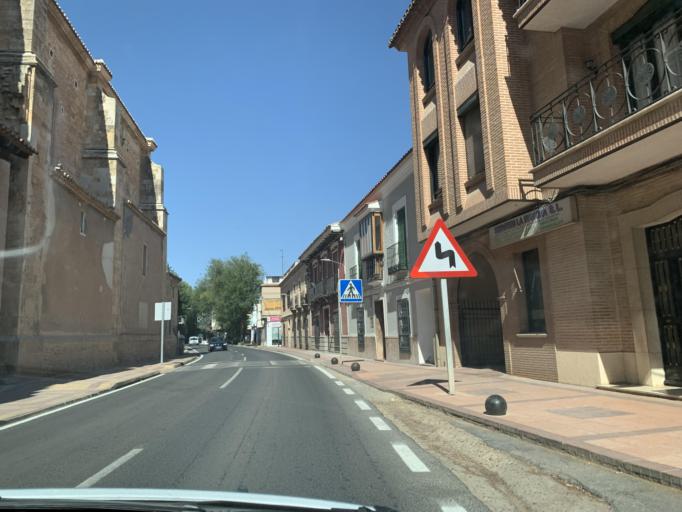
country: ES
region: Castille-La Mancha
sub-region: Provincia de Ciudad Real
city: Argamasilla de Alba
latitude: 39.1286
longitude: -3.0889
